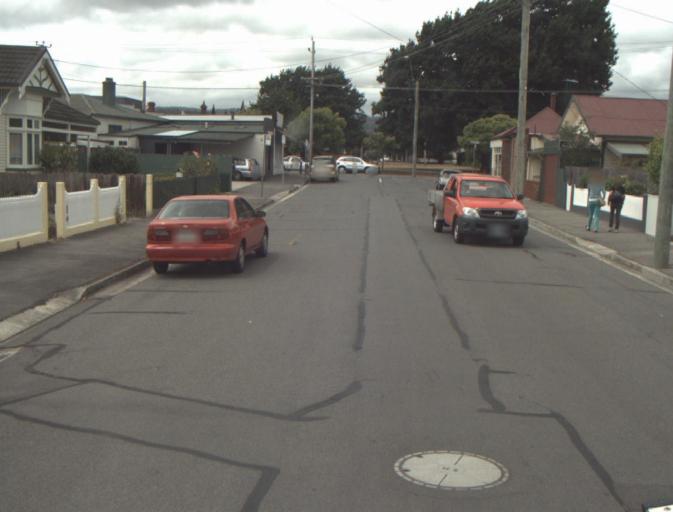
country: AU
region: Tasmania
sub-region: Launceston
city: Launceston
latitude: -41.4197
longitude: 147.1341
